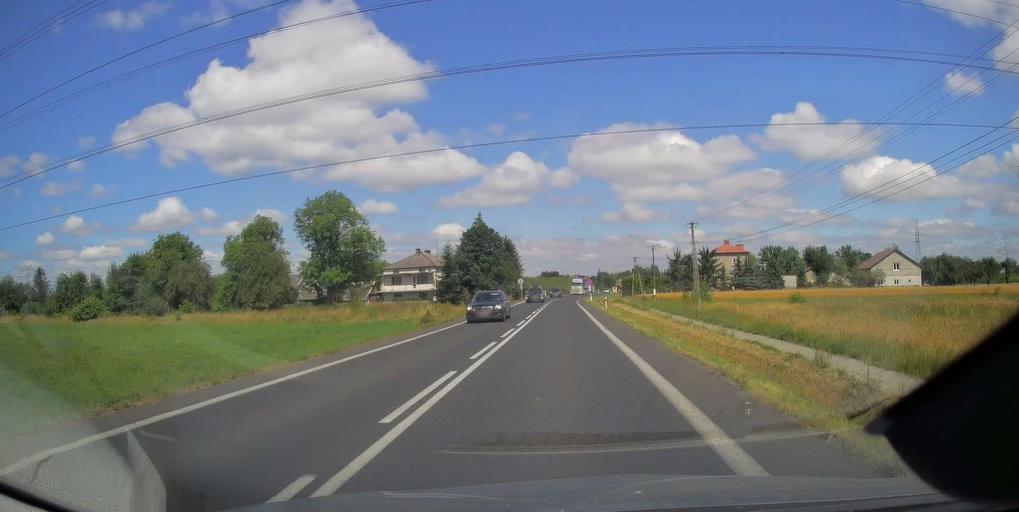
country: PL
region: Subcarpathian Voivodeship
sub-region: Powiat debicki
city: Brzeznica
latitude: 50.1267
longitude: 21.4857
